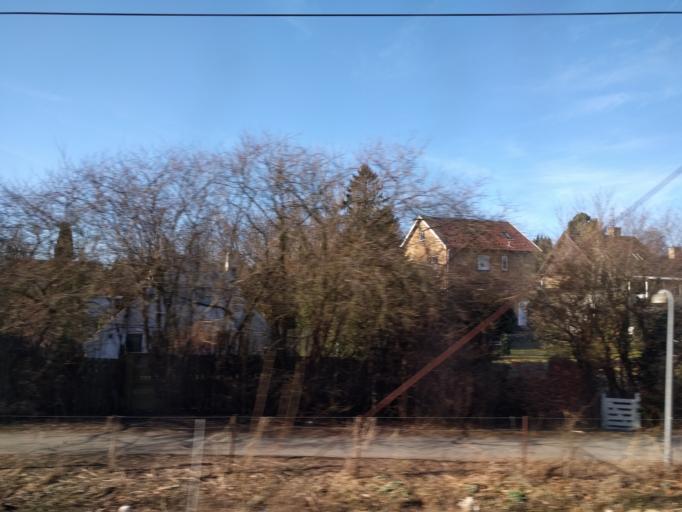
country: DK
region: Capital Region
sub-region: Horsholm Kommune
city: Horsholm
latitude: 55.8894
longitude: 12.5215
